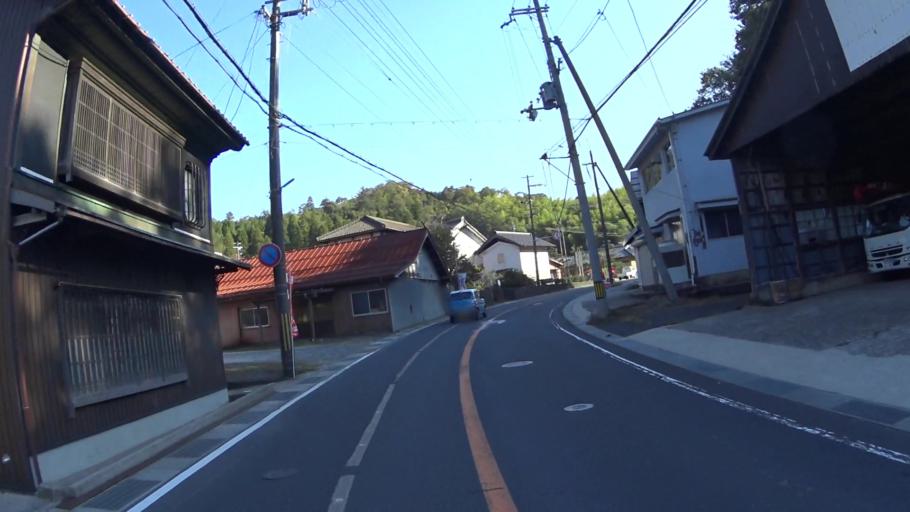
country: JP
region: Kyoto
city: Miyazu
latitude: 35.6199
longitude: 135.0612
